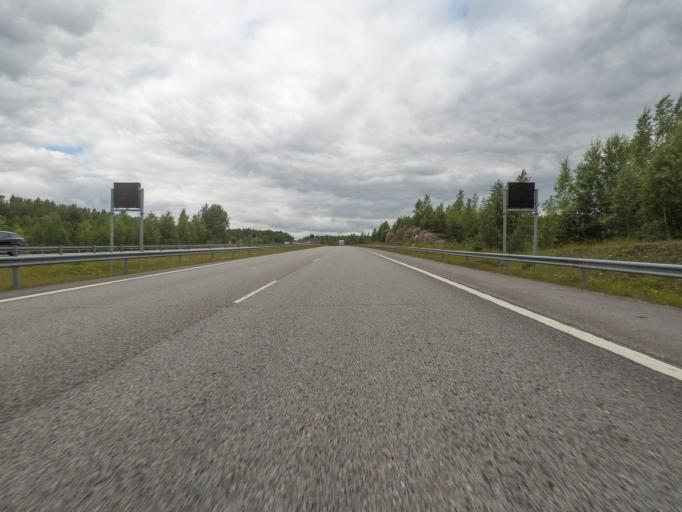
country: FI
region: Varsinais-Suomi
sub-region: Salo
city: Halikko
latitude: 60.4332
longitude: 22.9880
